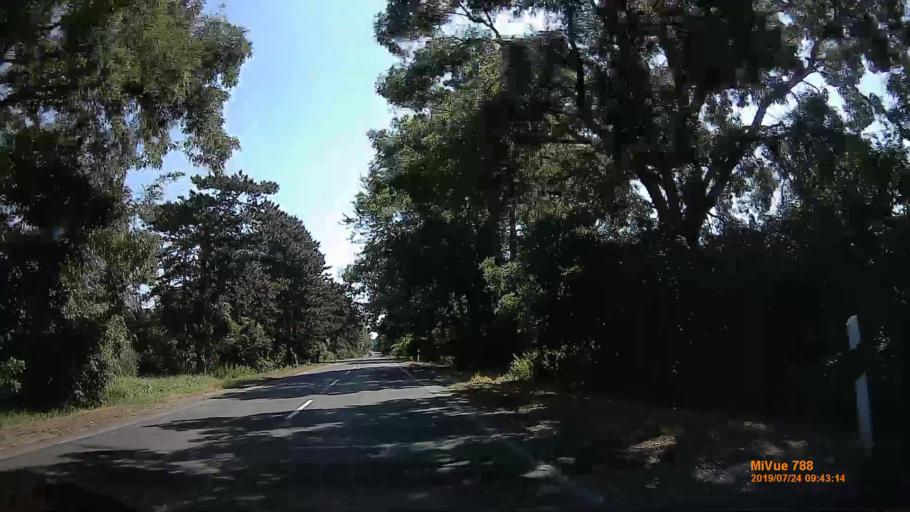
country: HU
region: Szabolcs-Szatmar-Bereg
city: Levelek
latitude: 47.9757
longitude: 22.0254
